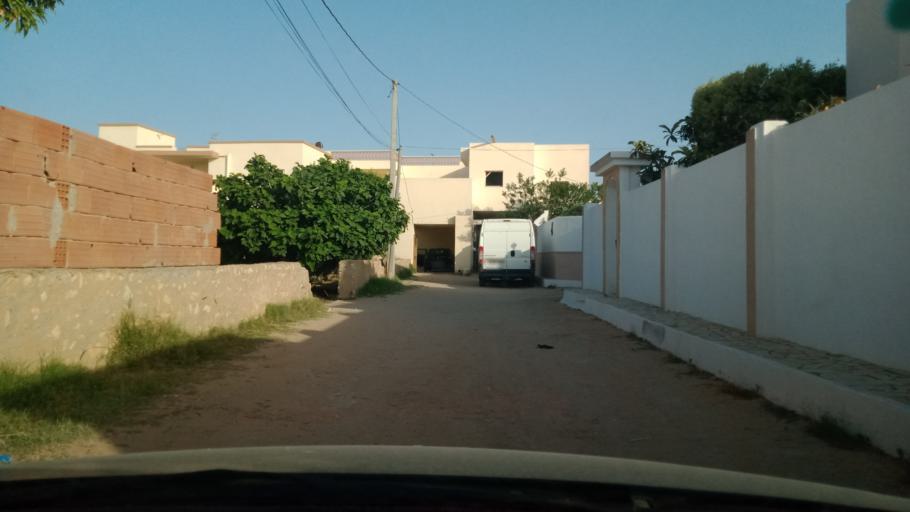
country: TN
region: Safaqis
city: Al Qarmadah
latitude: 34.8191
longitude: 10.7462
